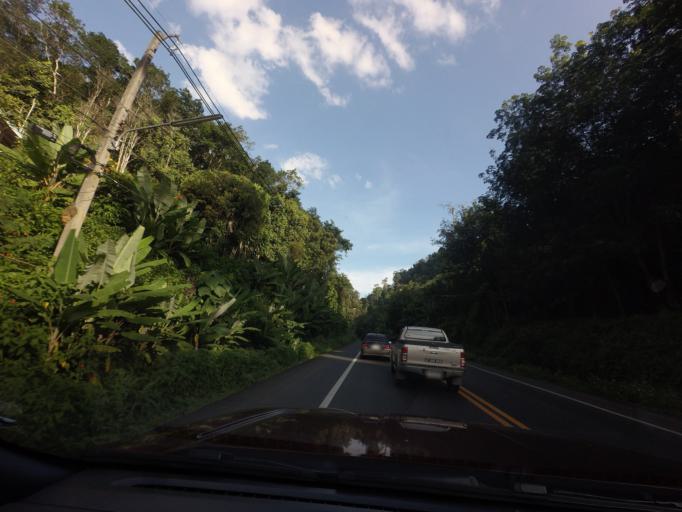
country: TH
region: Yala
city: Than To
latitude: 6.2075
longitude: 101.1689
